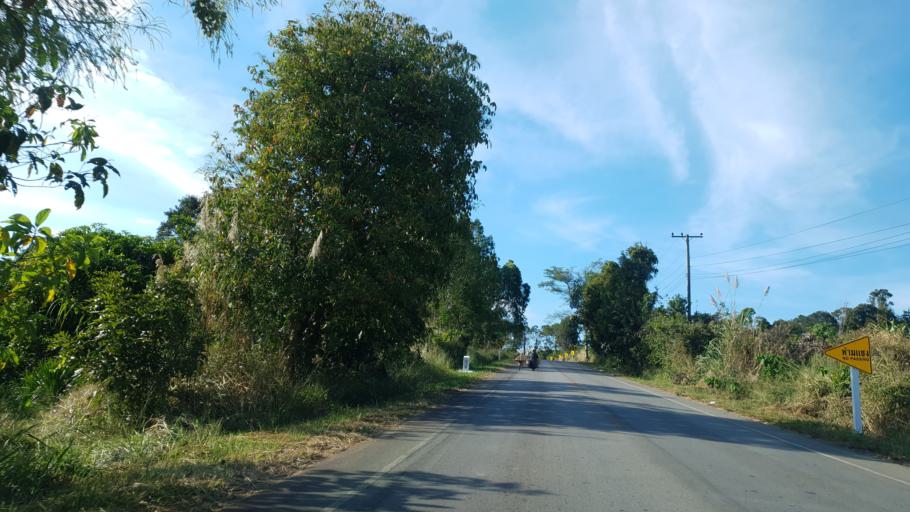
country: TH
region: Loei
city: Phu Ruea
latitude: 17.4444
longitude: 101.4999
